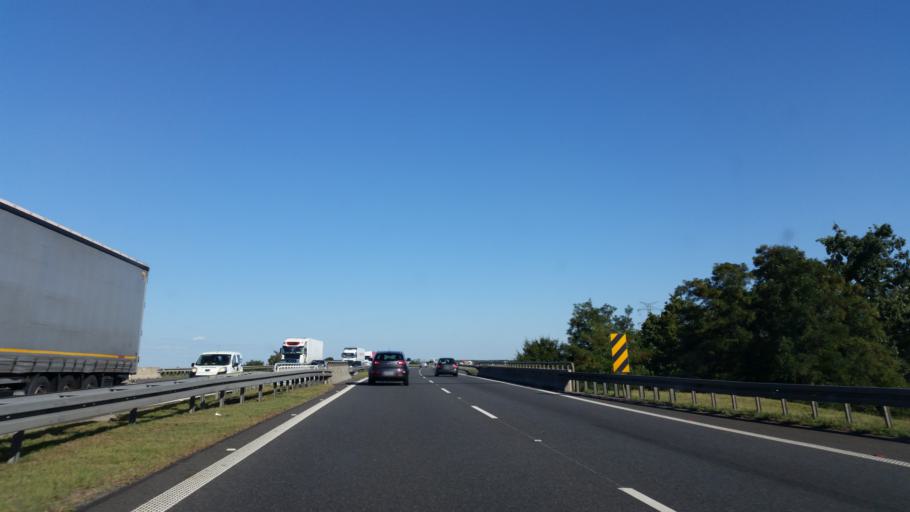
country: PL
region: Lower Silesian Voivodeship
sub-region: Powiat strzelinski
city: Wiazow
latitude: 50.8369
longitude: 17.2779
